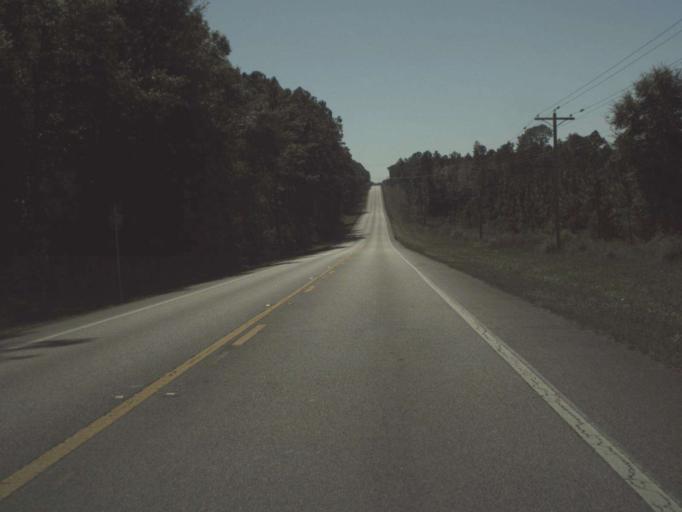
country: US
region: Florida
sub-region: Walton County
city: DeFuniak Springs
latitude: 30.9060
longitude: -86.1319
